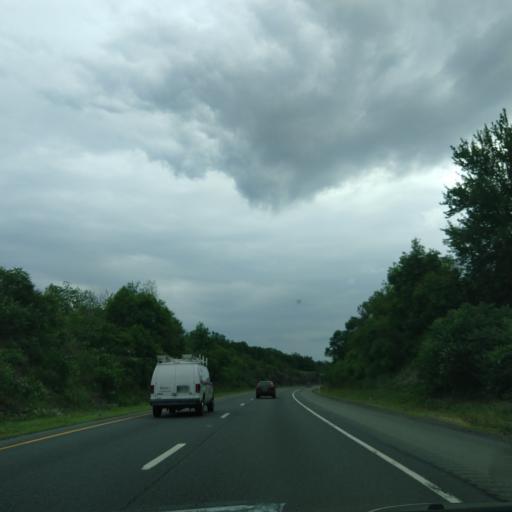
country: US
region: Pennsylvania
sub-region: Luzerne County
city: Laflin
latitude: 41.2771
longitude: -75.7956
